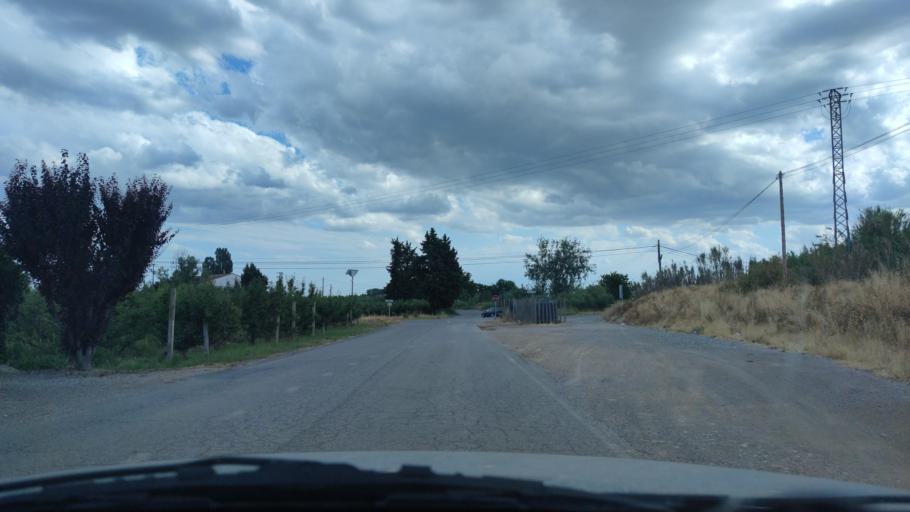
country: ES
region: Catalonia
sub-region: Provincia de Lleida
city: Lleida
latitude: 41.6112
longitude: 0.5829
